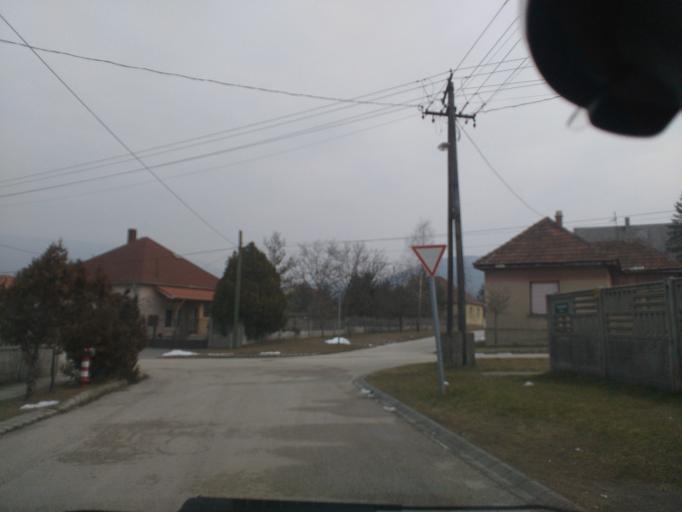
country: HU
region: Komarom-Esztergom
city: Piliscsev
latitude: 47.6715
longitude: 18.8159
